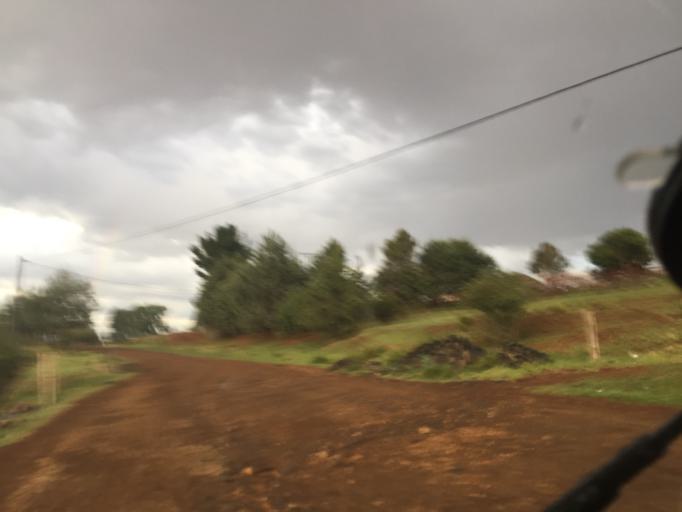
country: LS
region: Leribe
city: Leribe
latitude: -29.1569
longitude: 28.0349
